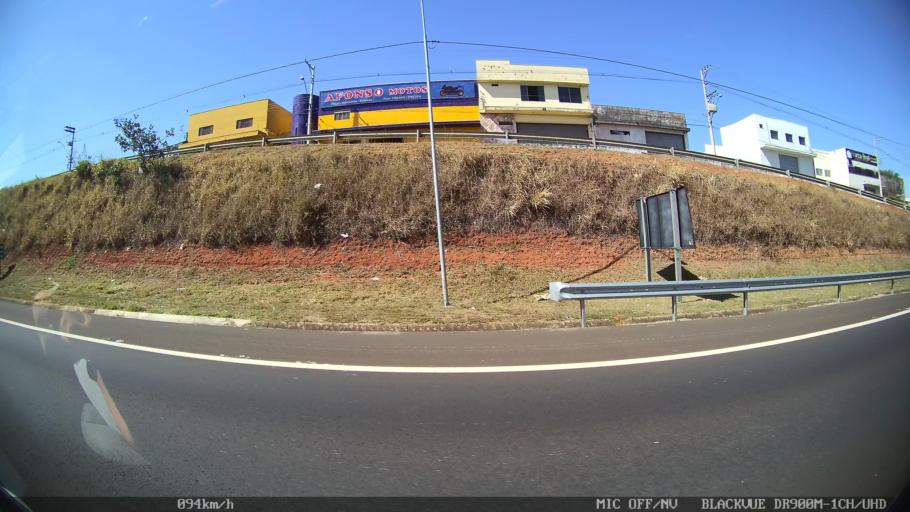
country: BR
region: Sao Paulo
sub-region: Franca
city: Franca
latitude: -20.5041
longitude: -47.4092
